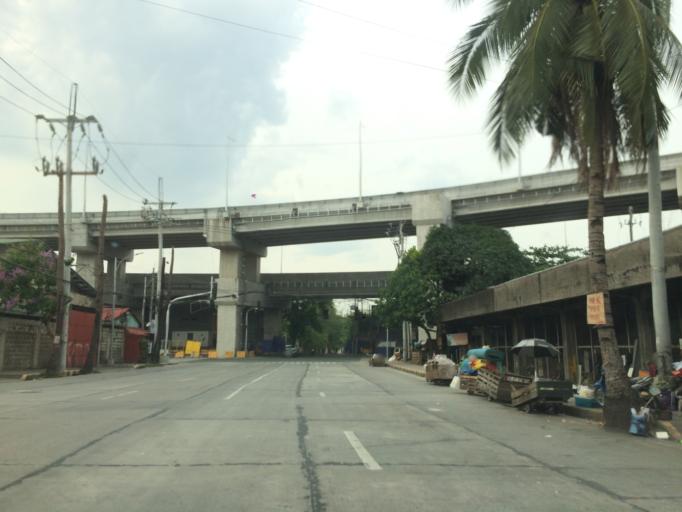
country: PH
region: Calabarzon
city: Del Monte
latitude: 14.6439
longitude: 121.0050
